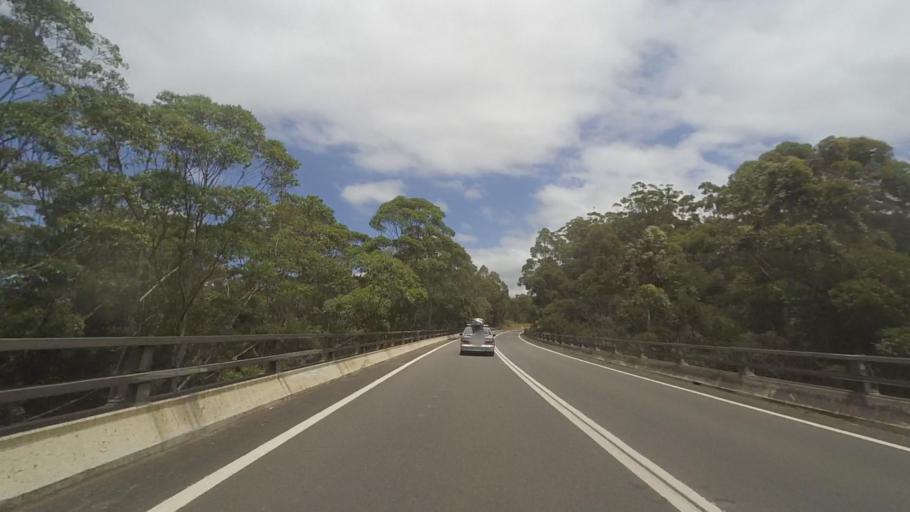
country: AU
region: New South Wales
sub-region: Shoalhaven Shire
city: Milton
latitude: -35.2395
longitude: 150.4300
